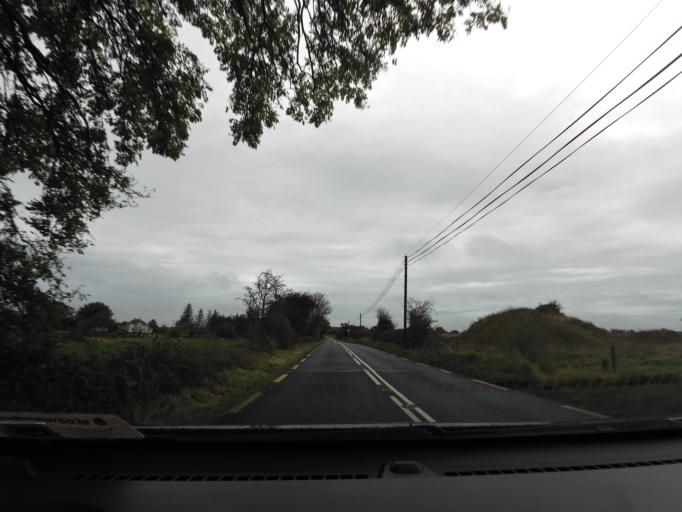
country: IE
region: Connaught
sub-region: County Galway
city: Tuam
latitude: 53.6025
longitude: -8.7593
